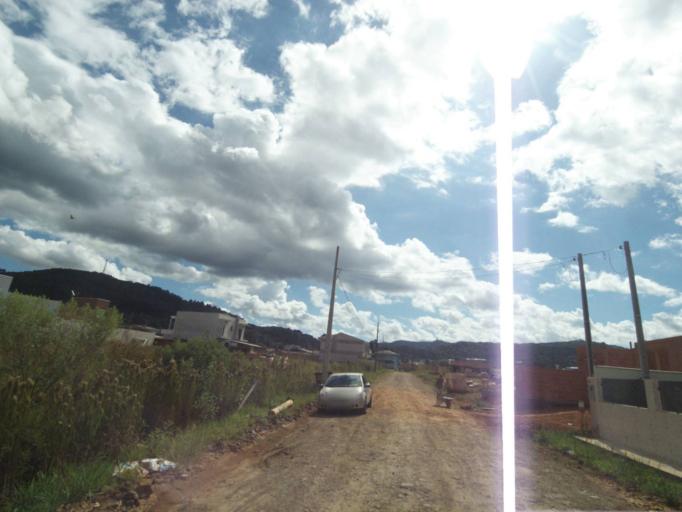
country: BR
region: Parana
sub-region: Uniao Da Vitoria
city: Uniao da Vitoria
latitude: -26.1505
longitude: -51.5406
